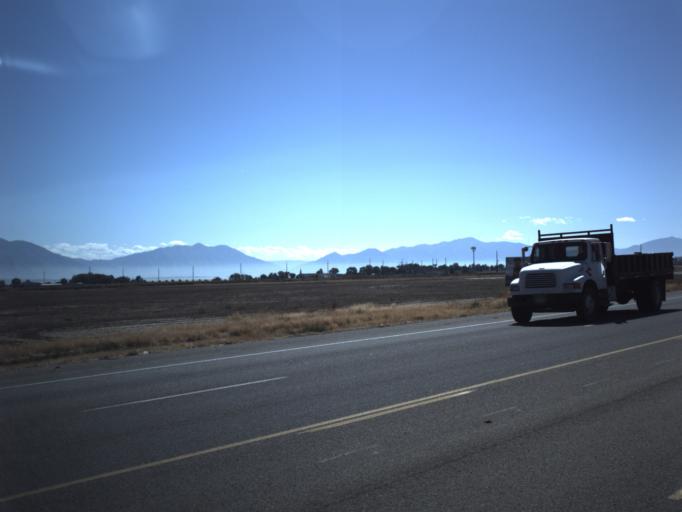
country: US
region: Utah
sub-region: Utah County
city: Saratoga Springs
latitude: 40.3631
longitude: -111.9163
